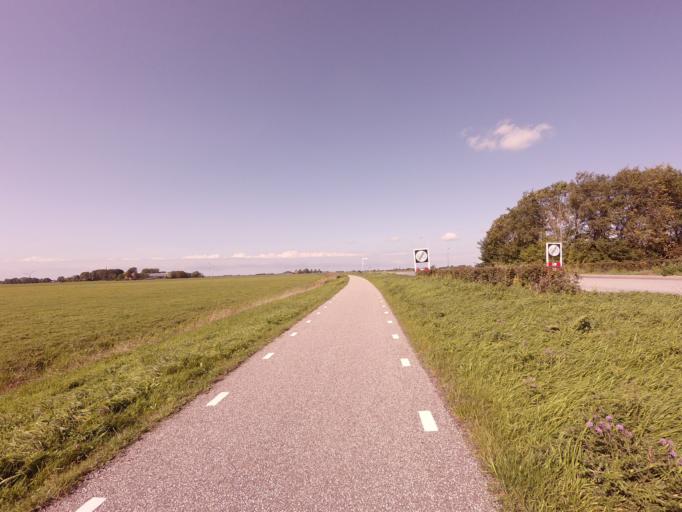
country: NL
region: Friesland
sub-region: Gemeente Littenseradiel
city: Makkum
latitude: 53.1099
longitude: 5.6872
